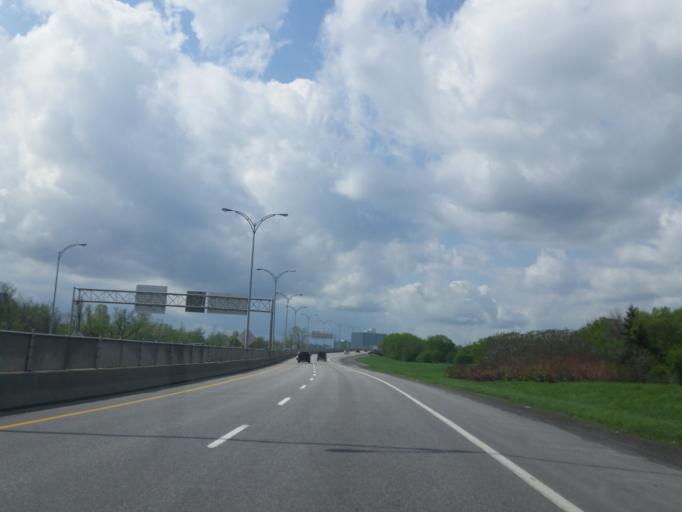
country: CA
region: Quebec
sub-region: Outaouais
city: Gatineau
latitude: 45.4452
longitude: -75.7218
